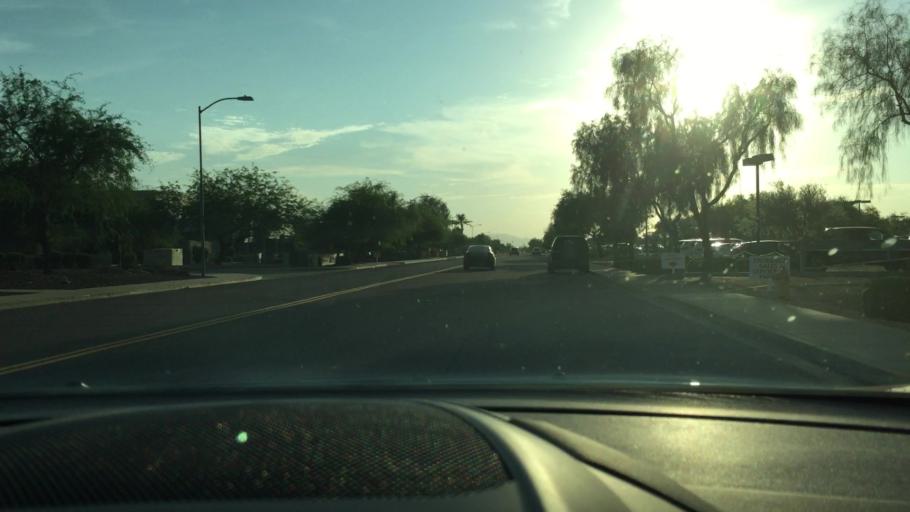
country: US
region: Arizona
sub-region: Maricopa County
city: Sun City
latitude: 33.6355
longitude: -112.2431
